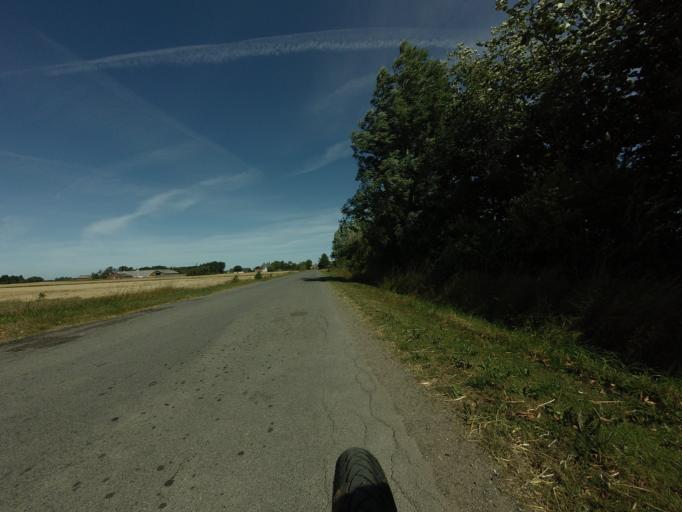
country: DK
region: North Denmark
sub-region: Hjorring Kommune
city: Vra
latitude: 57.3278
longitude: 9.8219
